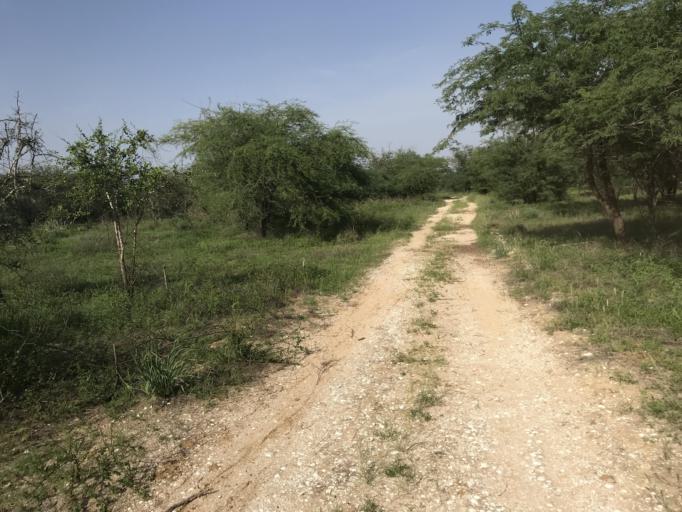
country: SN
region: Saint-Louis
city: Saint-Louis
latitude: 15.9302
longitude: -16.4671
